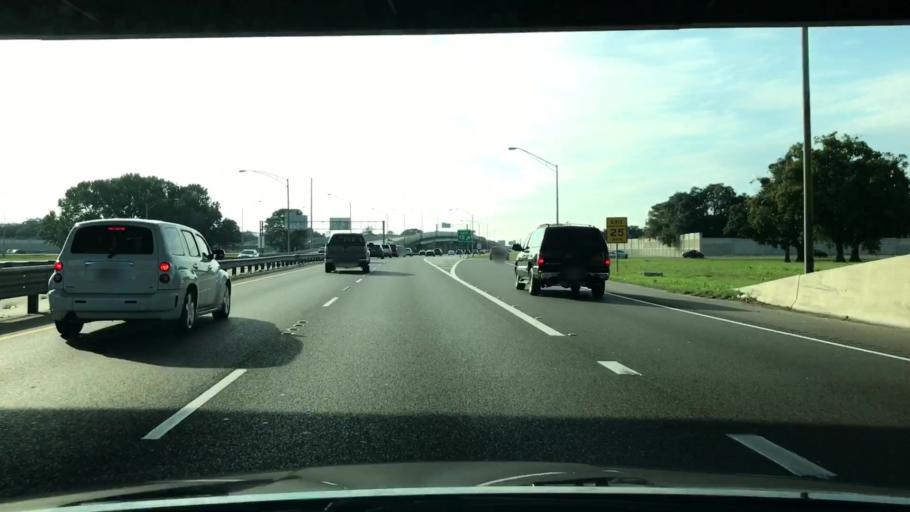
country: US
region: Louisiana
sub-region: Jefferson Parish
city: Metairie
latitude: 29.9958
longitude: -90.1158
